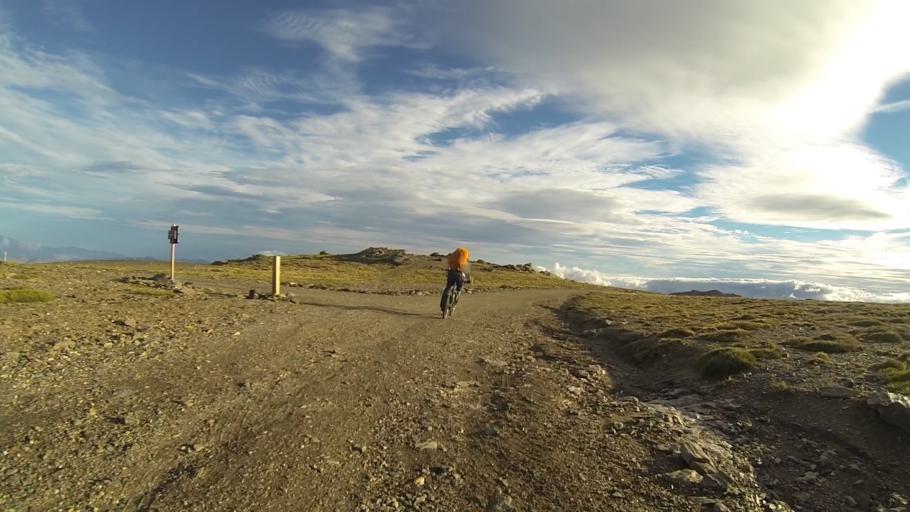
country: ES
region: Andalusia
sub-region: Provincia de Granada
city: Trevelez
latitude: 37.0096
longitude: -3.3026
